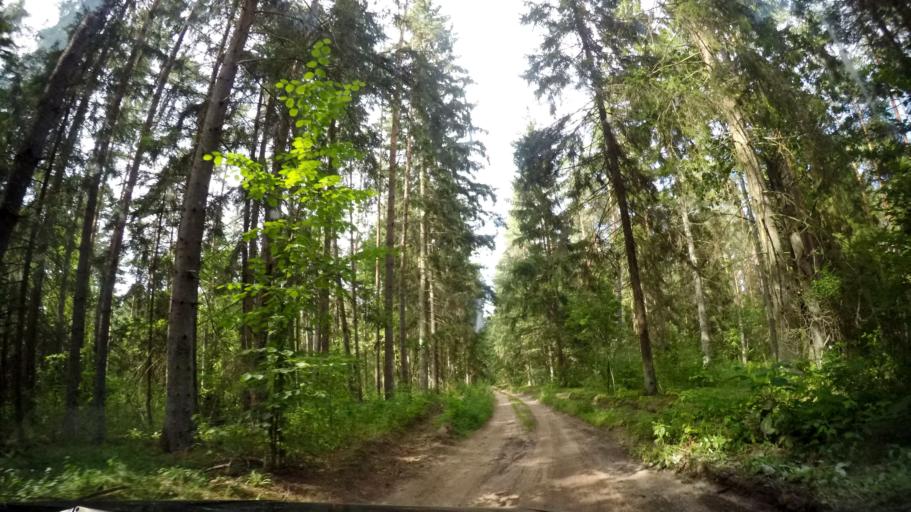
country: BY
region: Grodnenskaya
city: Skidal'
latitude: 53.8316
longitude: 24.1772
